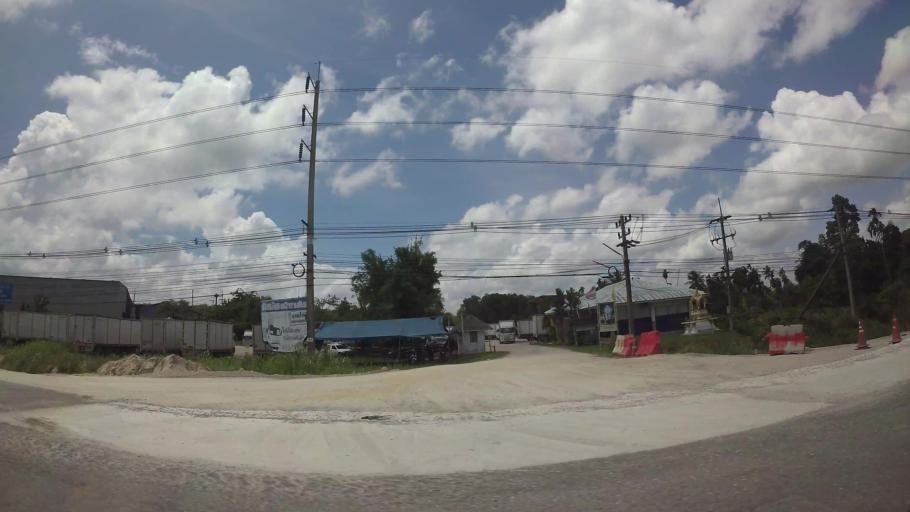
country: TH
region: Rayong
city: Nikhom Phattana
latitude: 12.7828
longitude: 101.1624
